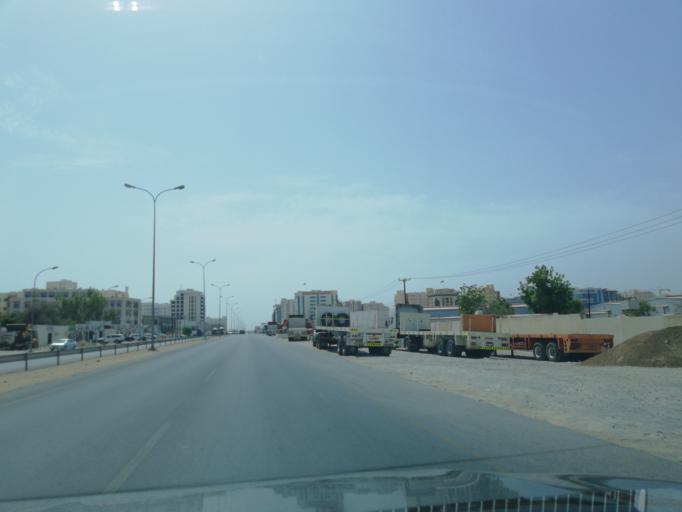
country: OM
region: Muhafazat Masqat
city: Bawshar
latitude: 23.5824
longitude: 58.3782
